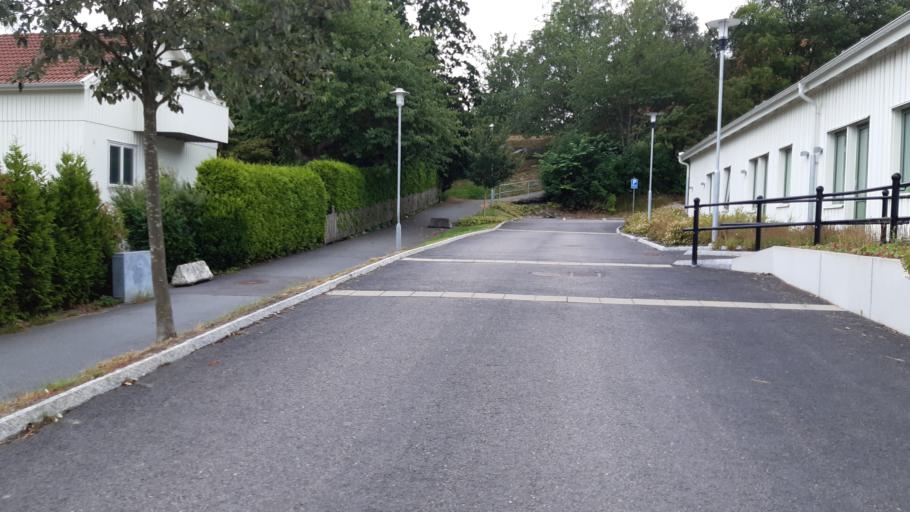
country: SE
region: Vaestra Goetaland
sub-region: Goteborg
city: Eriksbo
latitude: 57.7209
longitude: 12.0345
